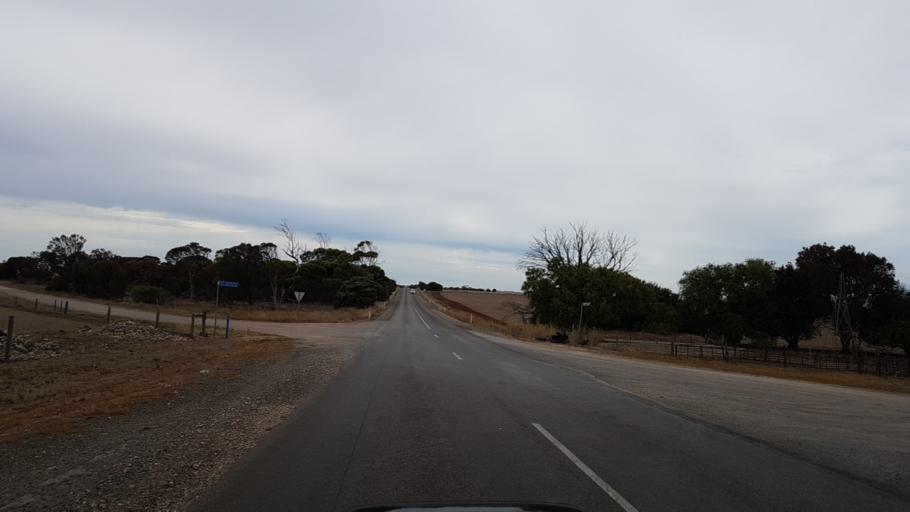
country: AU
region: South Australia
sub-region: Yorke Peninsula
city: Honiton
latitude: -34.9849
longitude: 137.2962
